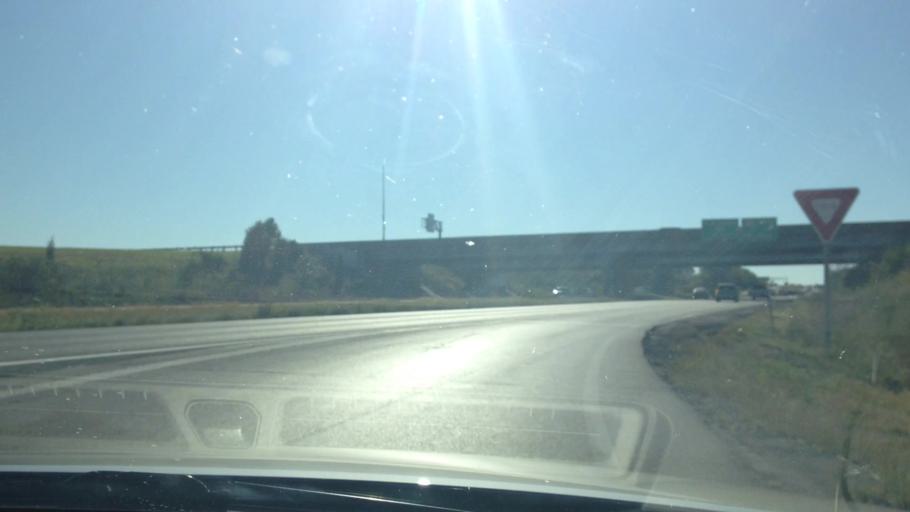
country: US
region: Missouri
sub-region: Clay County
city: Pleasant Valley
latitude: 39.2436
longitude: -94.5058
